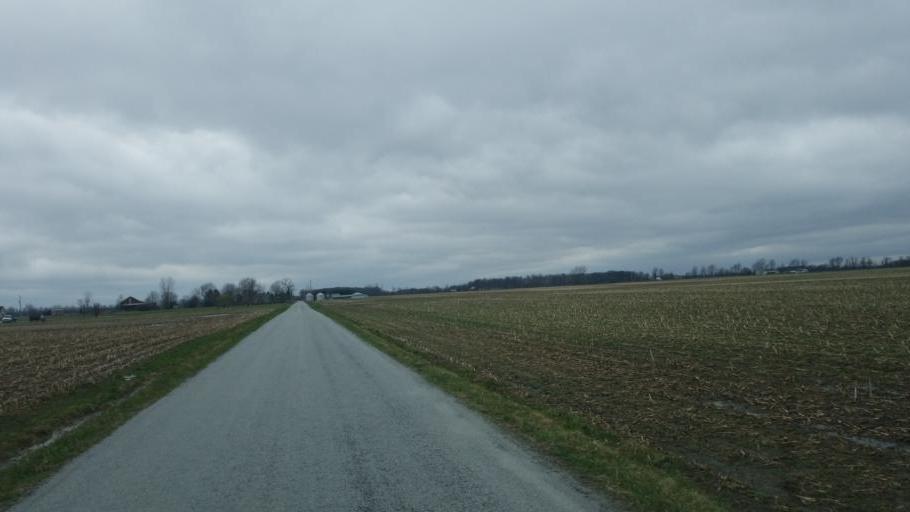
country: US
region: Ohio
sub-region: Hardin County
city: Forest
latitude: 40.7307
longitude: -83.5435
